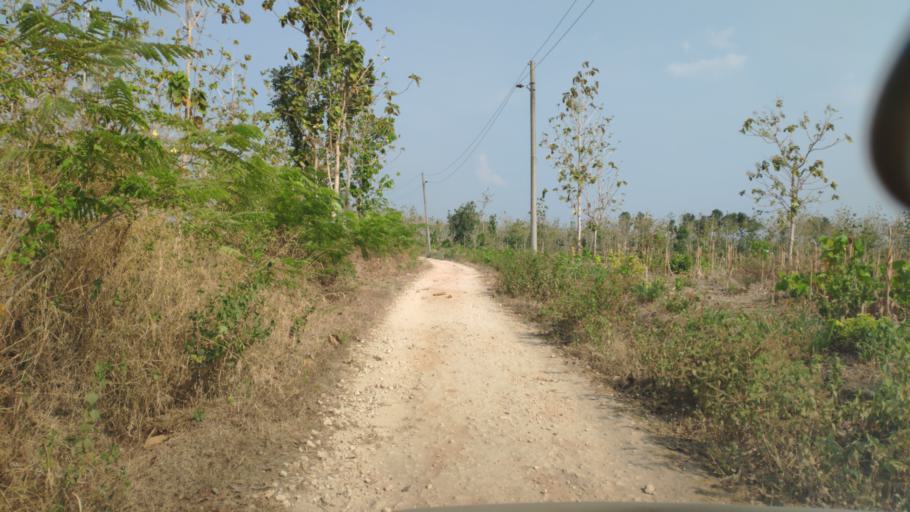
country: ID
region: Central Java
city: Jomblang
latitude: -7.0261
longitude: 111.4539
